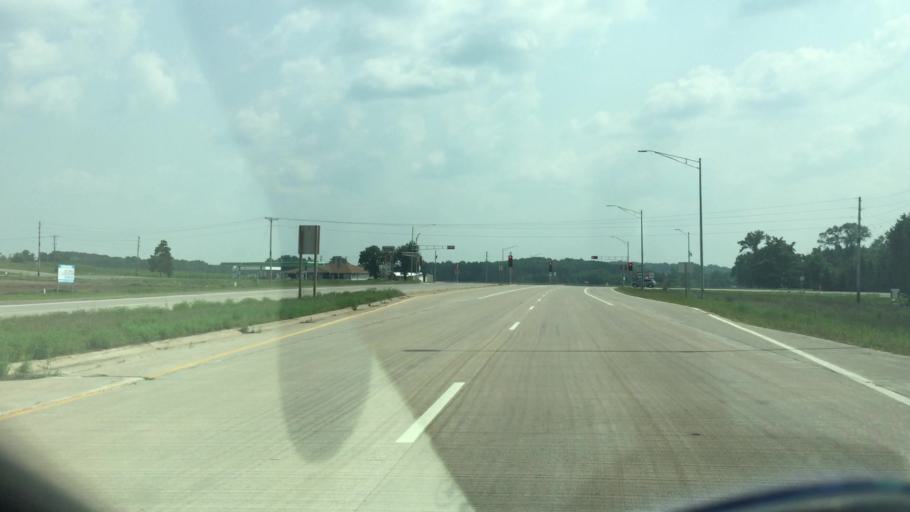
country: US
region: Wisconsin
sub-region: Eau Claire County
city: Altoona
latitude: 44.7429
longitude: -91.4497
